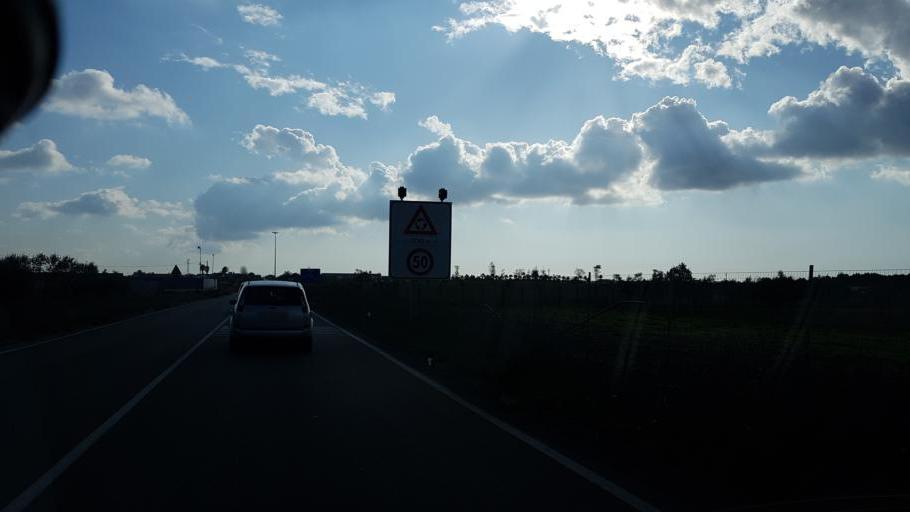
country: IT
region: Apulia
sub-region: Provincia di Lecce
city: Veglie
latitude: 40.3526
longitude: 17.9685
